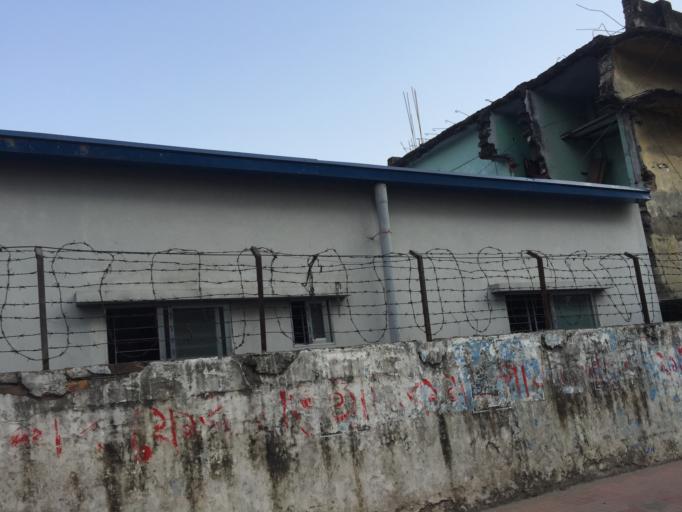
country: BD
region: Dhaka
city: Azimpur
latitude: 23.7582
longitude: 90.3859
